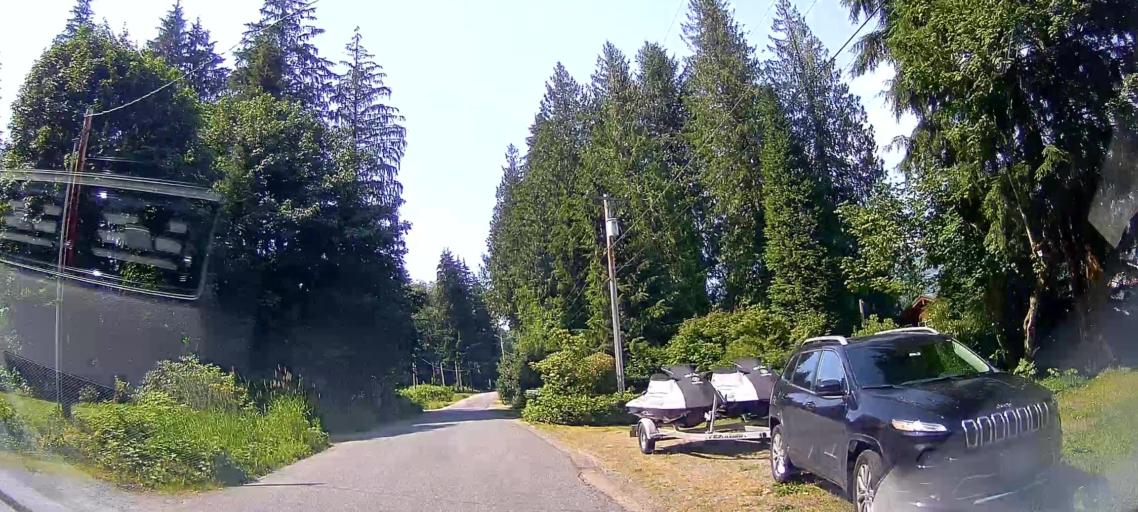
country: US
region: Washington
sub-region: Snohomish County
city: Arlington Heights
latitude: 48.3196
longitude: -122.0301
